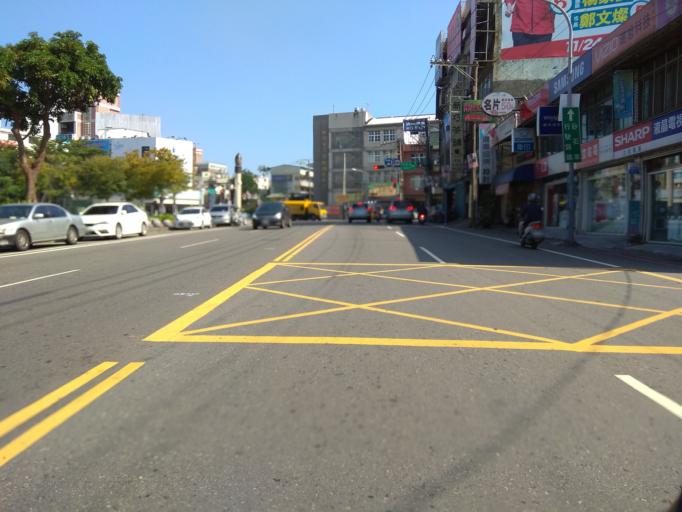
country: TW
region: Taiwan
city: Taoyuan City
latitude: 24.9507
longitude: 121.2176
